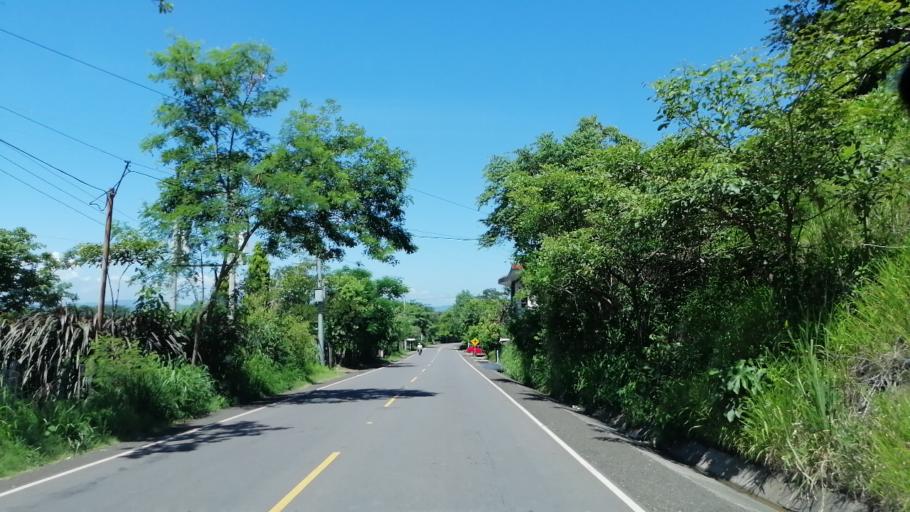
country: SV
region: Morazan
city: Cacaopera
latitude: 13.8105
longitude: -88.1639
